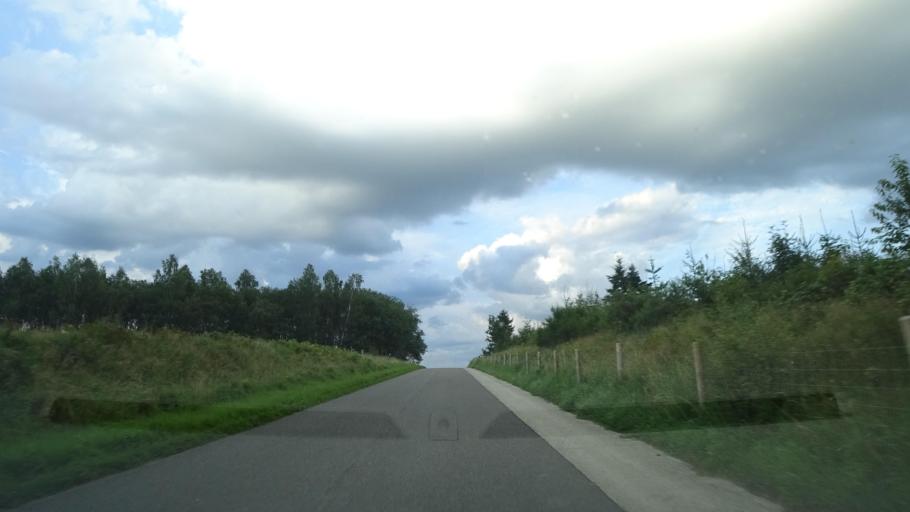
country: BE
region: Wallonia
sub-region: Province du Luxembourg
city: Bertrix
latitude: 49.8112
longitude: 5.3084
